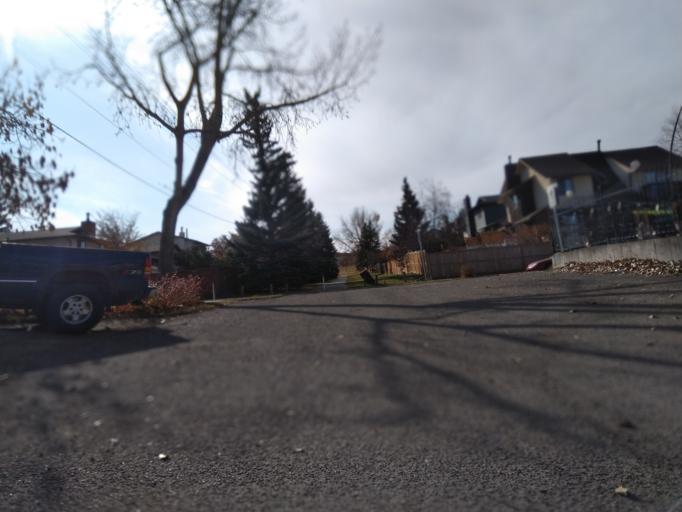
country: CA
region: Alberta
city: Calgary
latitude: 51.1273
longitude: -114.0851
